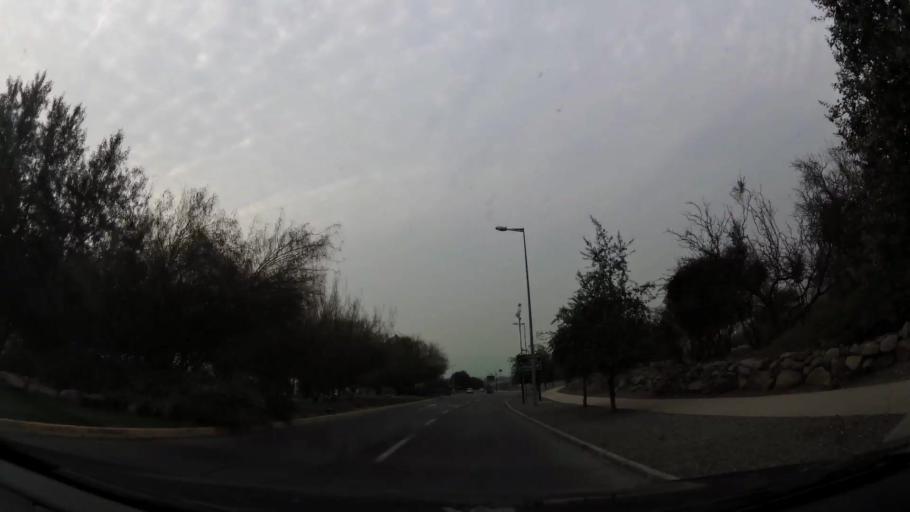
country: CL
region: Santiago Metropolitan
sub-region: Provincia de Chacabuco
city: Chicureo Abajo
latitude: -33.2738
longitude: -70.6251
